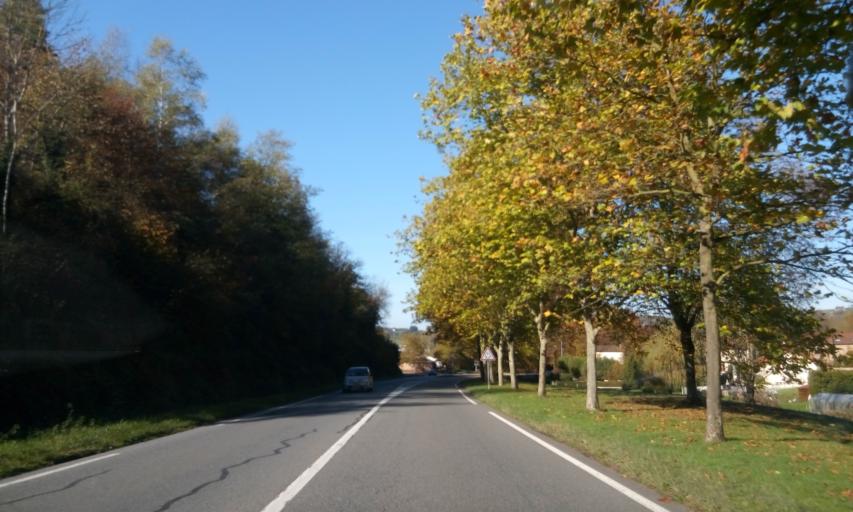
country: FR
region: Rhone-Alpes
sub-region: Departement du Rhone
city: Bourg-de-Thizy
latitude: 46.0309
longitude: 4.2986
